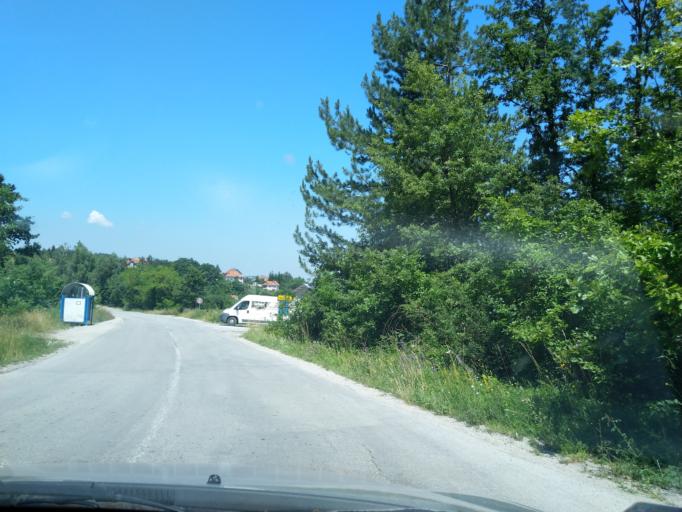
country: RS
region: Central Serbia
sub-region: Zlatiborski Okrug
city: Uzice
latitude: 43.8034
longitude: 19.8160
